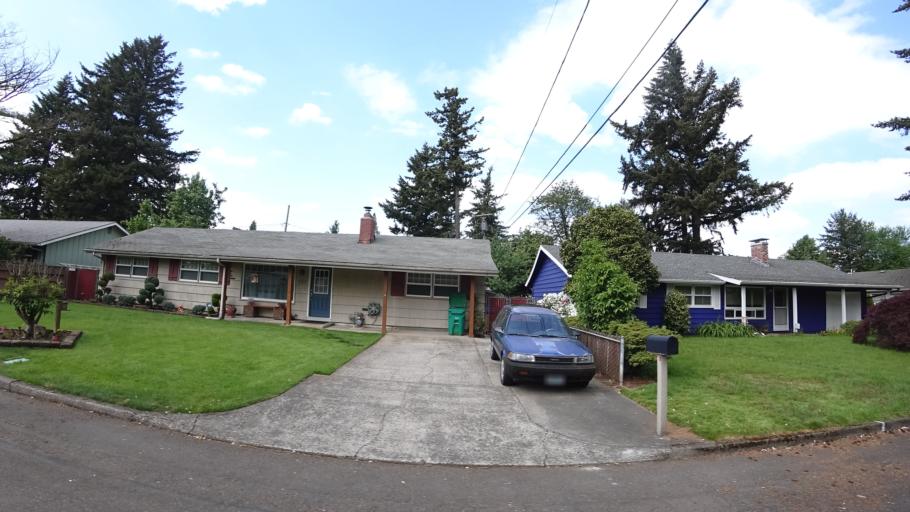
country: US
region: Oregon
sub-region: Multnomah County
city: Fairview
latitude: 45.5178
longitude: -122.4797
